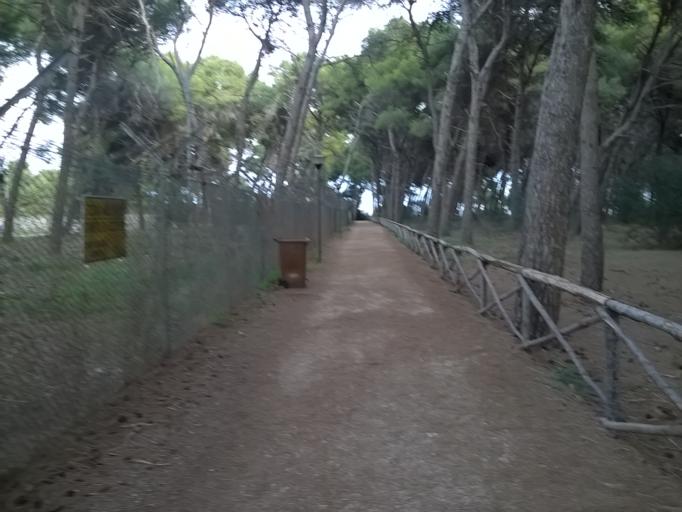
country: IT
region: Apulia
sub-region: Provincia di Taranto
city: Paolo VI
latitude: 40.4670
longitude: 17.2984
